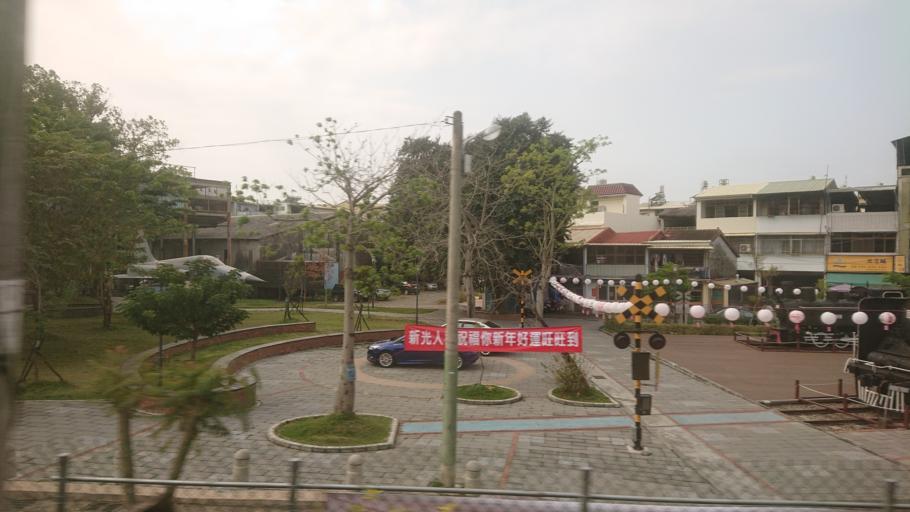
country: TW
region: Taiwan
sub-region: Nantou
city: Nantou
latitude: 23.8145
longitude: 120.6166
